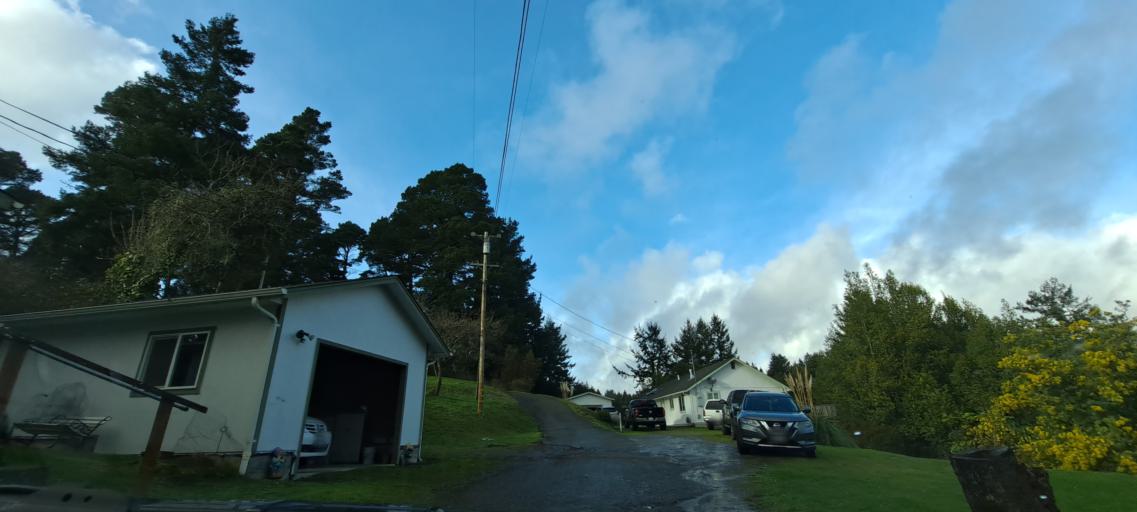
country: US
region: California
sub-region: Humboldt County
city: Fortuna
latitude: 40.6031
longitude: -124.1590
